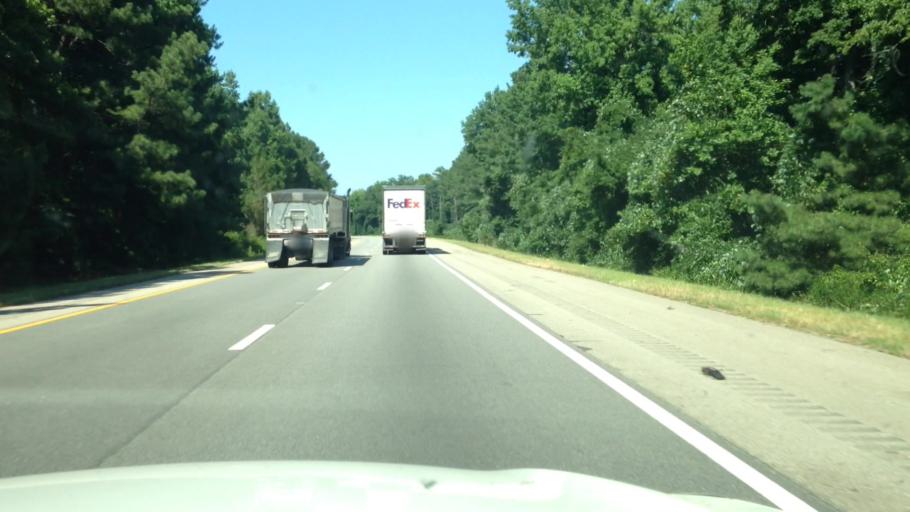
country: US
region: North Carolina
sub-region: Wilson County
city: Lucama
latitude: 35.6844
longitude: -78.0592
